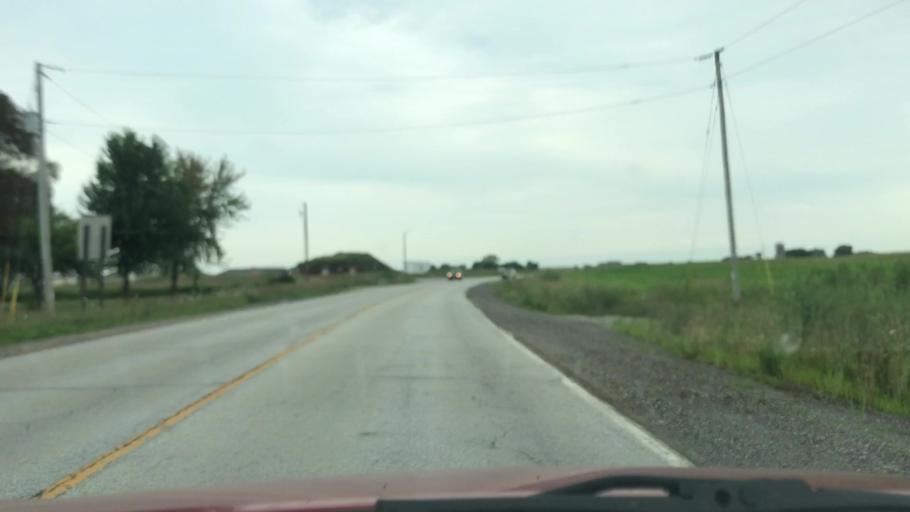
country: US
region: Wisconsin
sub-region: Brown County
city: De Pere
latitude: 44.4378
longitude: -88.1359
